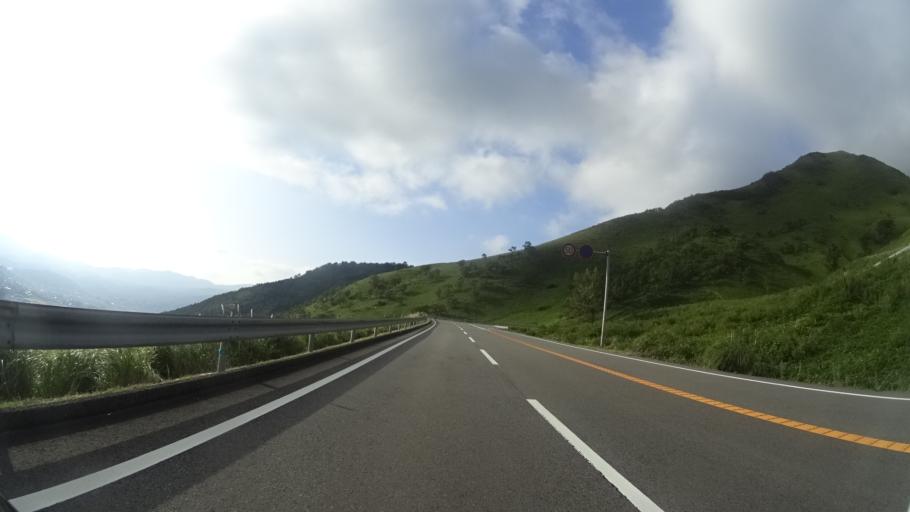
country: JP
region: Oita
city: Beppu
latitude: 33.2637
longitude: 131.3830
